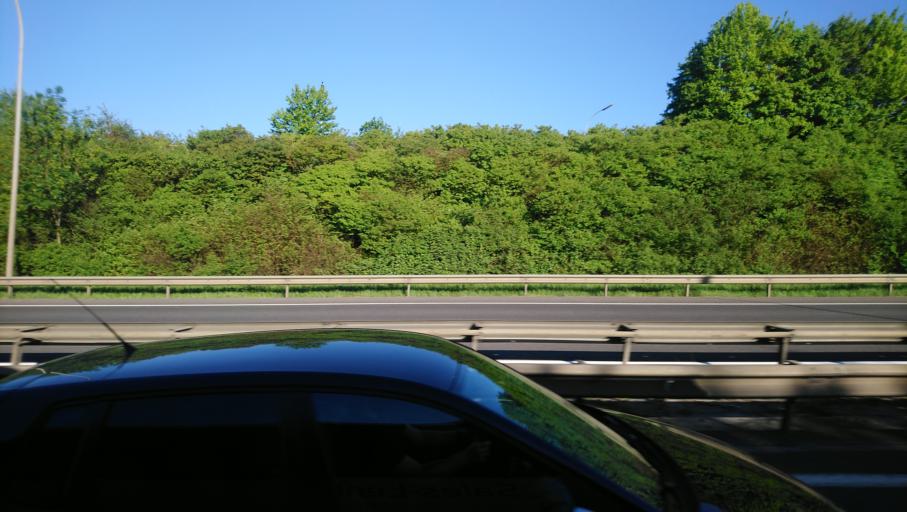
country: LU
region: Luxembourg
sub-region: Canton d'Esch-sur-Alzette
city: Leudelange
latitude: 49.5684
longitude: 6.0863
